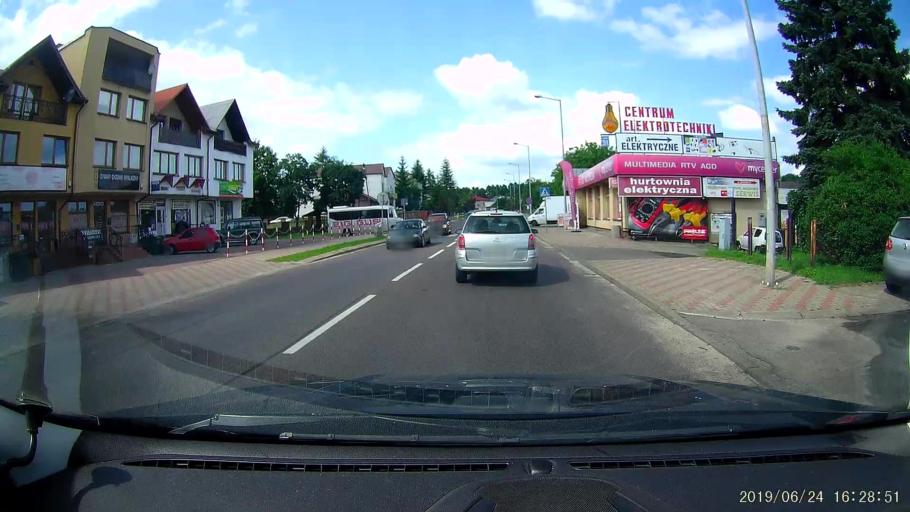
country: PL
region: Lublin Voivodeship
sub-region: Powiat tomaszowski
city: Tomaszow Lubelski
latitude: 50.4558
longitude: 23.4205
